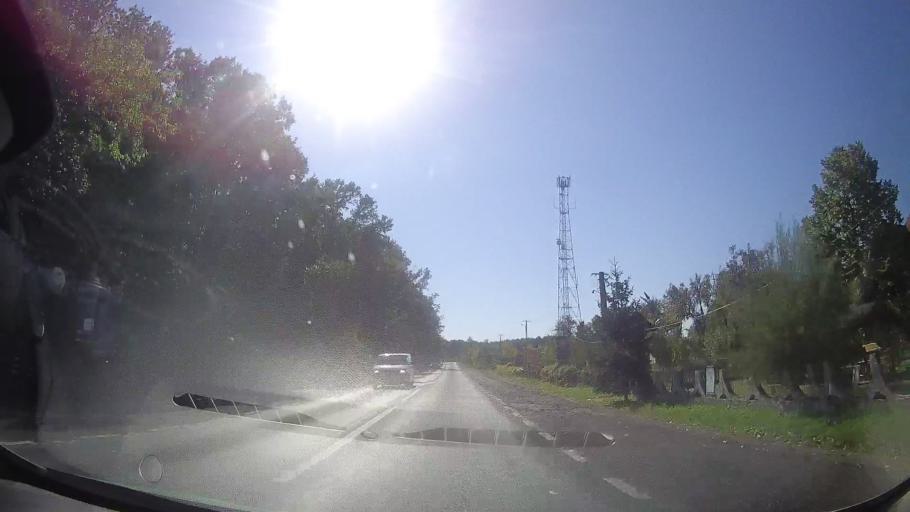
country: RO
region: Timis
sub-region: Comuna Barna
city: Barna
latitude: 45.7208
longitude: 21.9959
